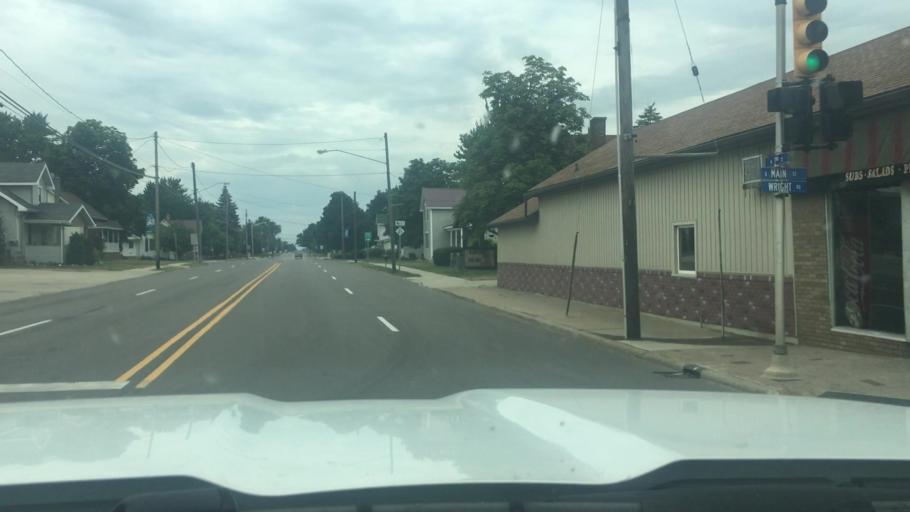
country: US
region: Michigan
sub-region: Clinton County
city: Fowler
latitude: 43.0019
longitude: -84.7398
